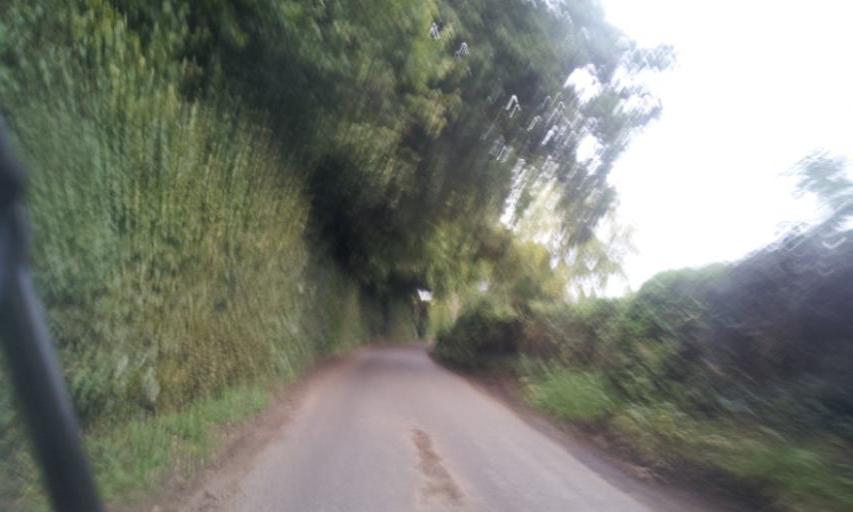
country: GB
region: England
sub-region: Kent
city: Aylesford
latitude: 51.2692
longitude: 0.4651
